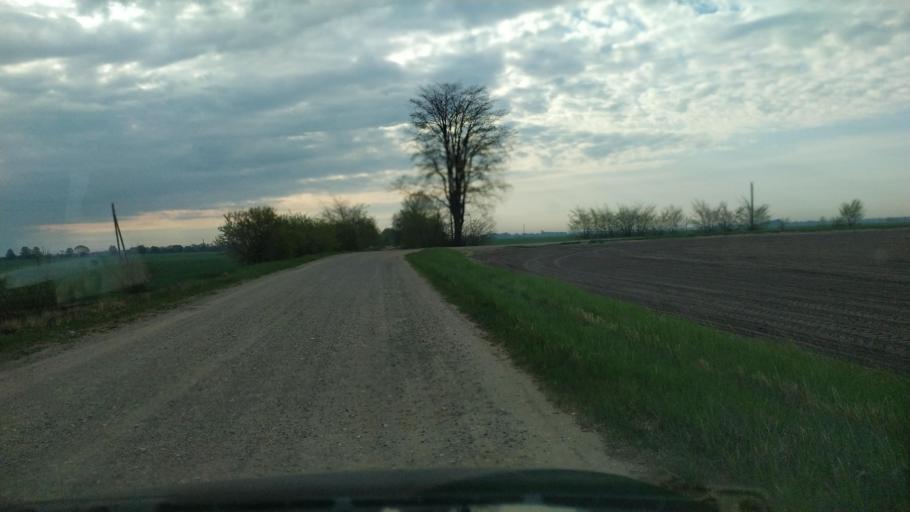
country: BY
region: Brest
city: Zhabinka
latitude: 52.1357
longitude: 24.0920
